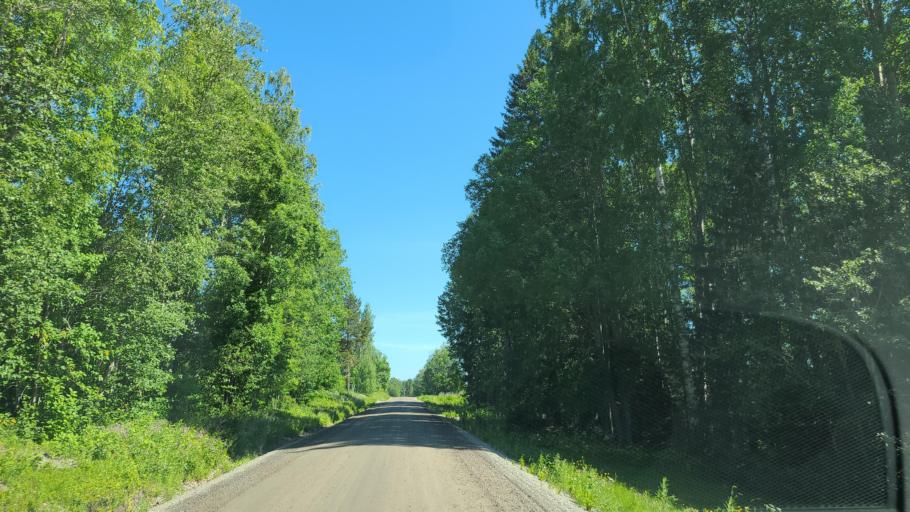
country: SE
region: Vaesterbotten
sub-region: Bjurholms Kommun
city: Bjurholm
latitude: 63.6782
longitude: 19.0050
